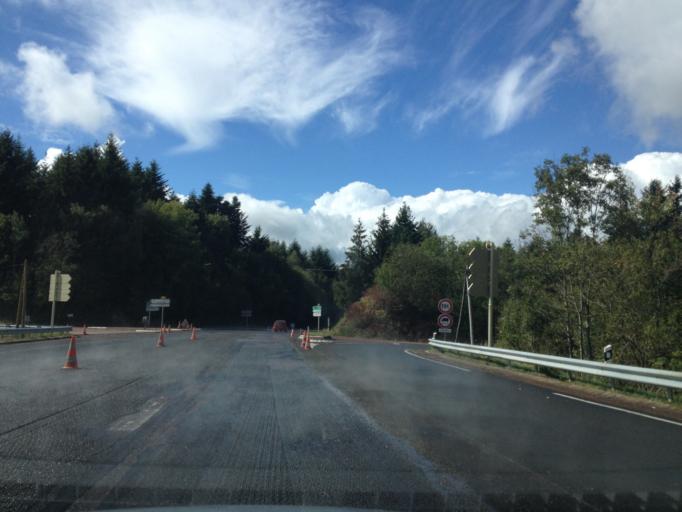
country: FR
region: Rhone-Alpes
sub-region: Departement du Rhone
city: Amplepuis
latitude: 45.9182
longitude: 4.3257
